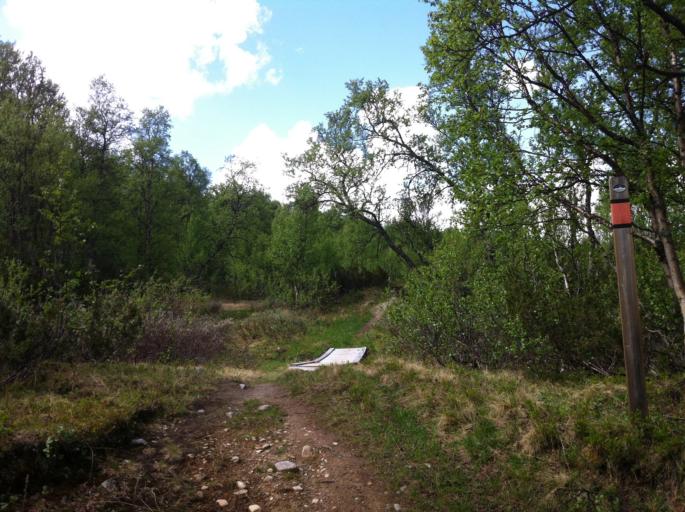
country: NO
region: Sor-Trondelag
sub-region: Tydal
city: Aas
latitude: 62.7132
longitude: 12.4847
